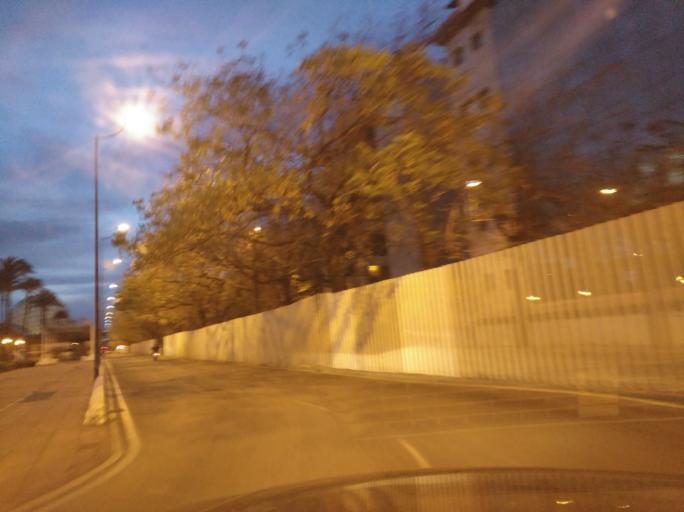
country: ES
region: Andalusia
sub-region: Provincia de Sevilla
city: Camas
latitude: 37.4058
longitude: -6.0037
